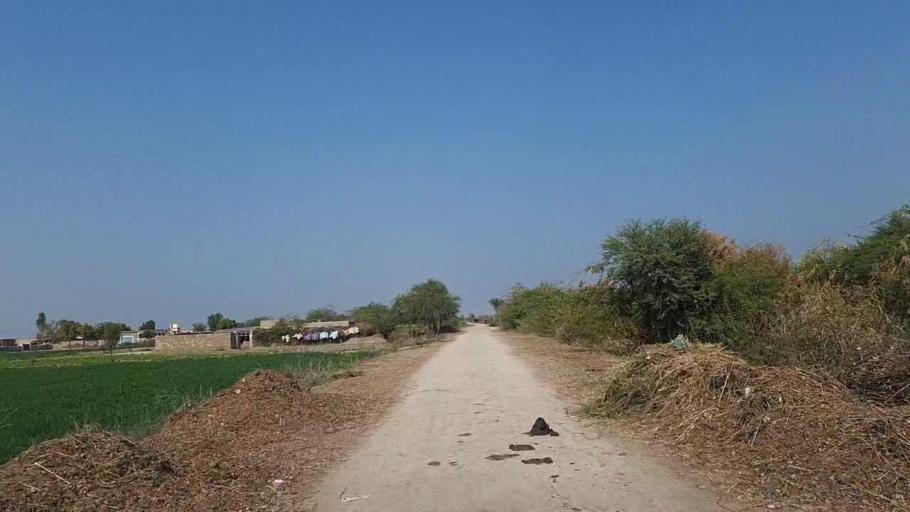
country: PK
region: Sindh
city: Nawabshah
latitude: 26.2779
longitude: 68.5135
